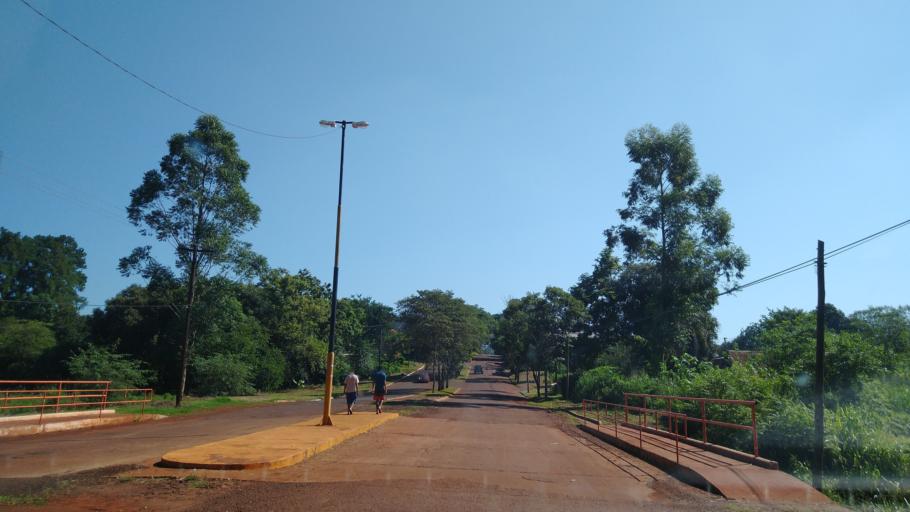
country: AR
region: Misiones
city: Puerto Esperanza
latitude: -26.0280
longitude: -54.6122
